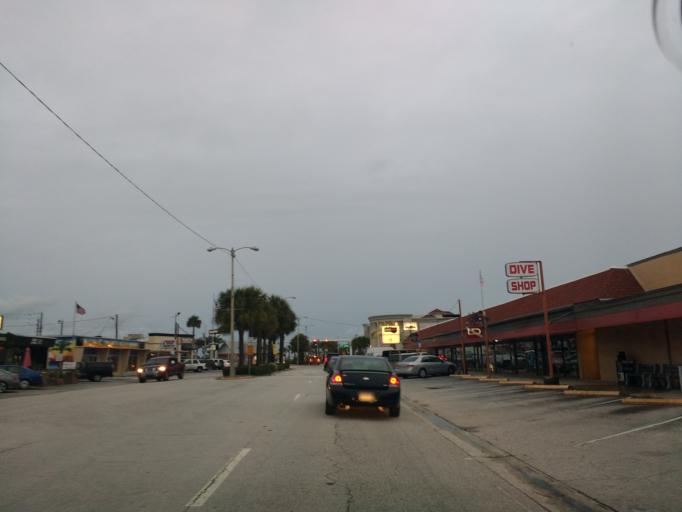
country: US
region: Florida
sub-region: Pinellas County
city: Madeira Beach
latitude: 27.8021
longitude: -82.8009
